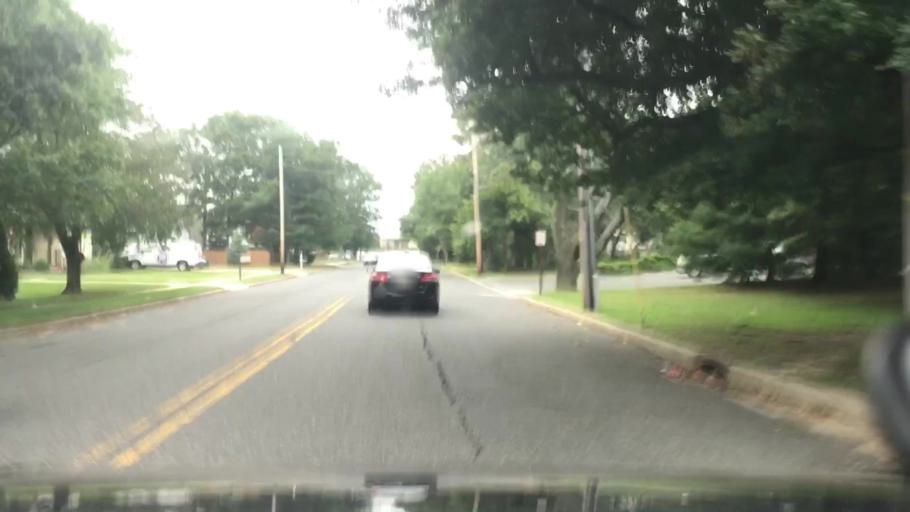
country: US
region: New Jersey
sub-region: Monmouth County
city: Eatontown
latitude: 40.2890
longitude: -74.0456
